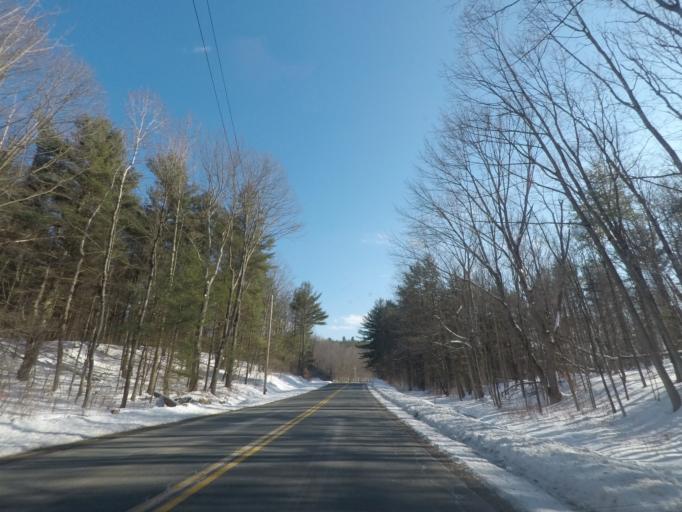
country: US
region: New York
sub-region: Rensselaer County
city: Hoosick Falls
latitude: 42.8922
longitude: -73.4960
